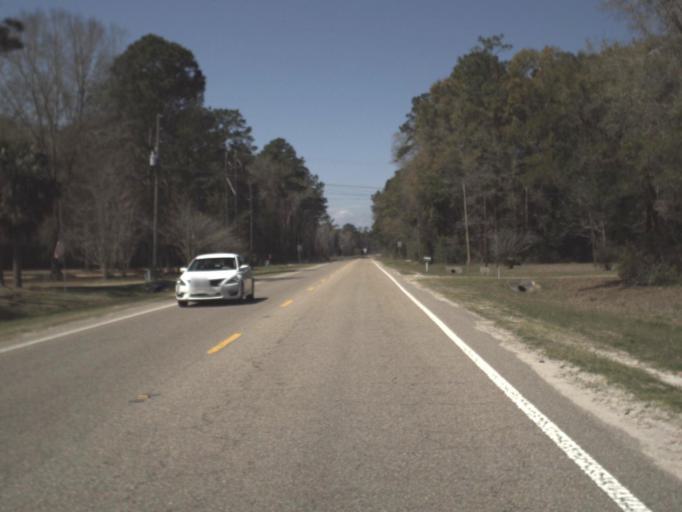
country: US
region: Florida
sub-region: Leon County
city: Woodville
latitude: 30.2287
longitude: -84.2205
